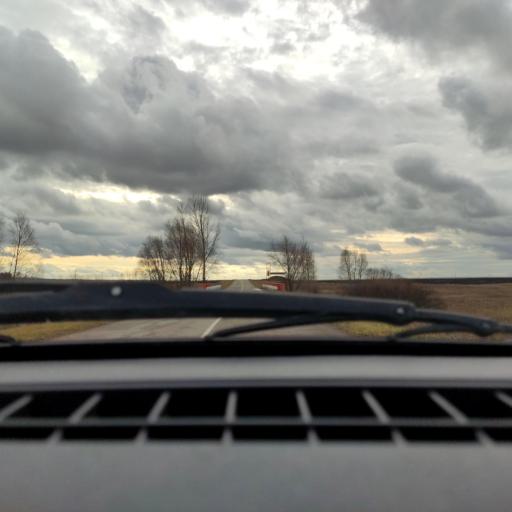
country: RU
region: Bashkortostan
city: Asanovo
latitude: 54.9451
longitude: 55.5206
